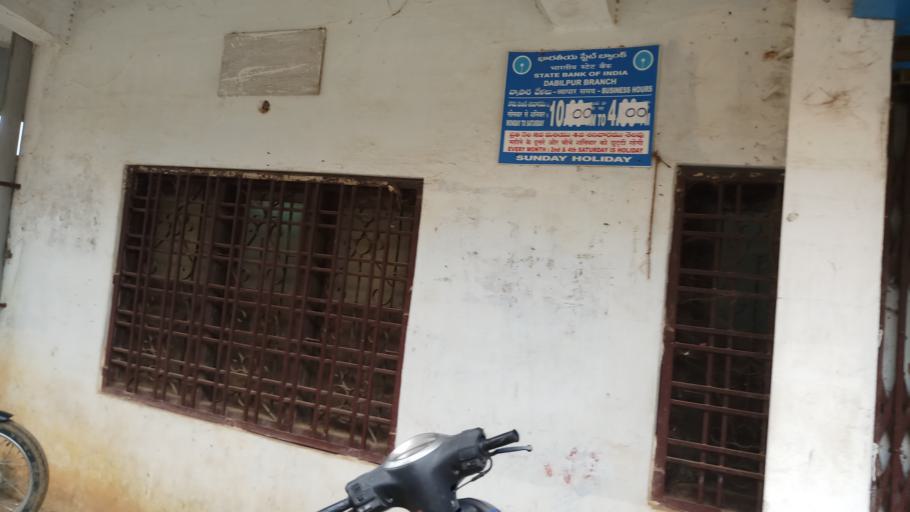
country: IN
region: Telangana
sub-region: Rangareddi
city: Quthbullapur
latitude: 17.6673
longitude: 78.4700
